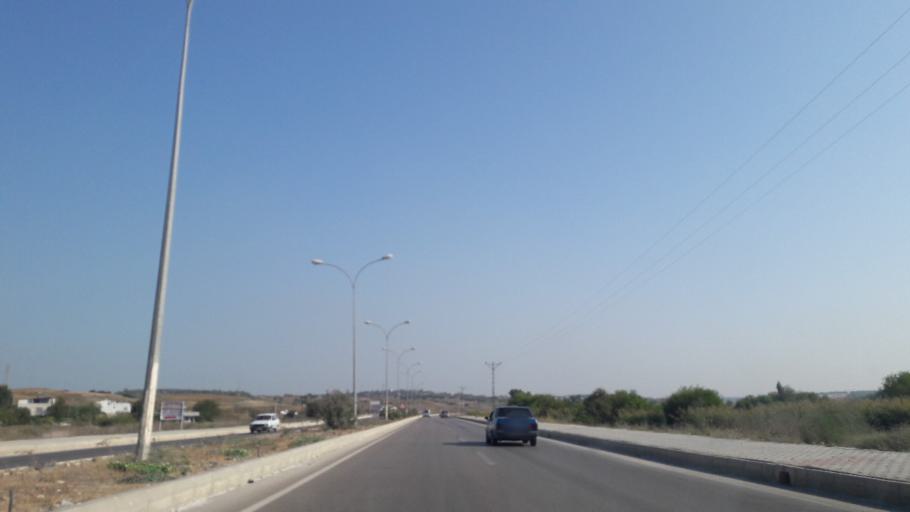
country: TR
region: Adana
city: Yuregir
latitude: 37.0582
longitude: 35.4430
